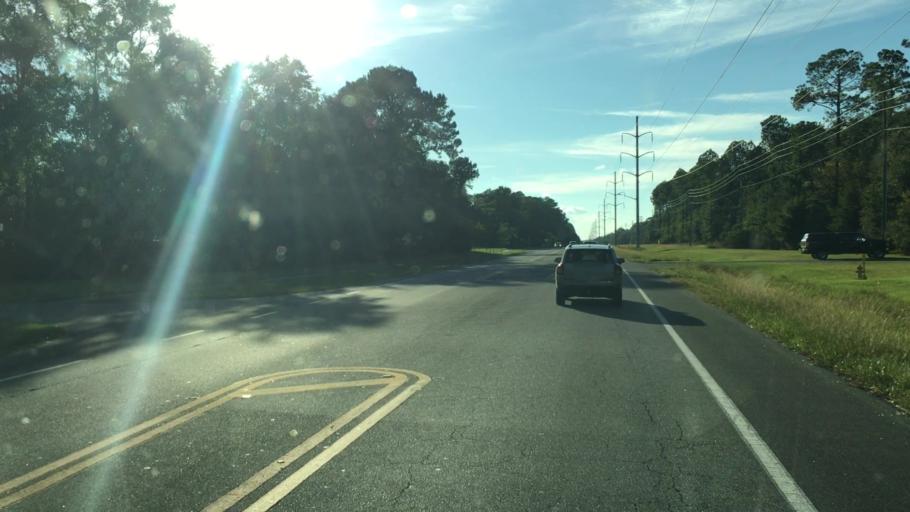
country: US
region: Florida
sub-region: Alachua County
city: Gainesville
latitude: 29.7033
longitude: -82.3512
